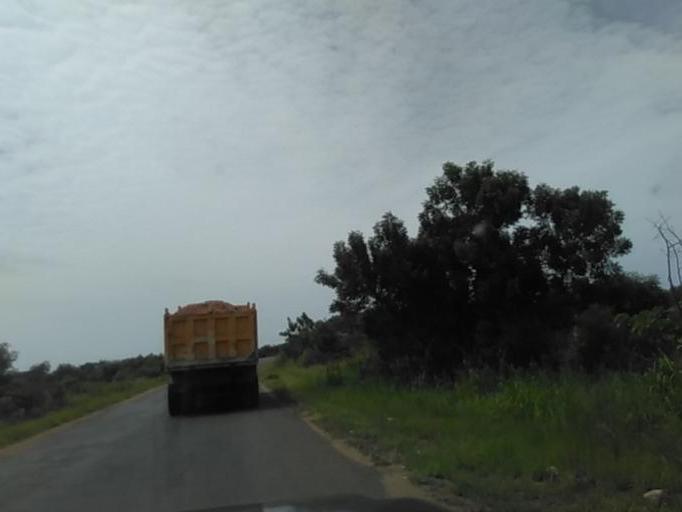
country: GH
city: Akropong
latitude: 6.0946
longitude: 0.0607
